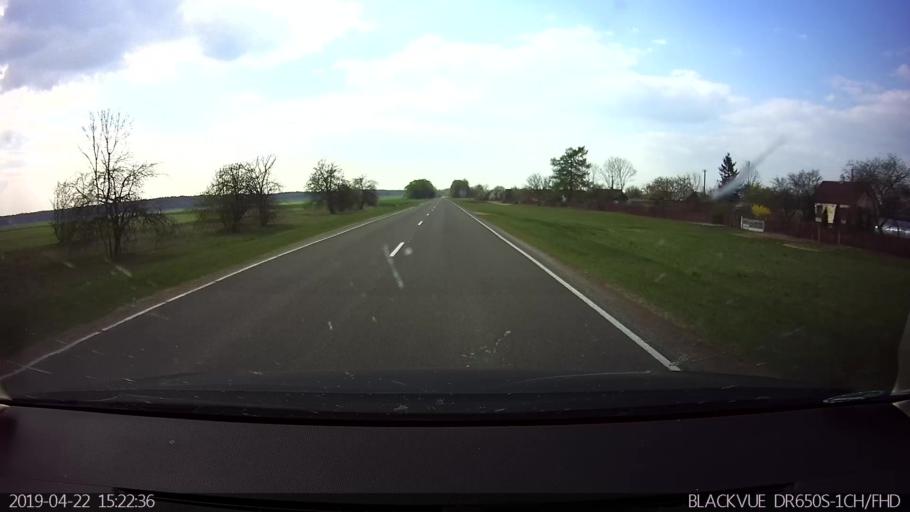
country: BY
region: Brest
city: Vysokaye
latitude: 52.3508
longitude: 23.4426
